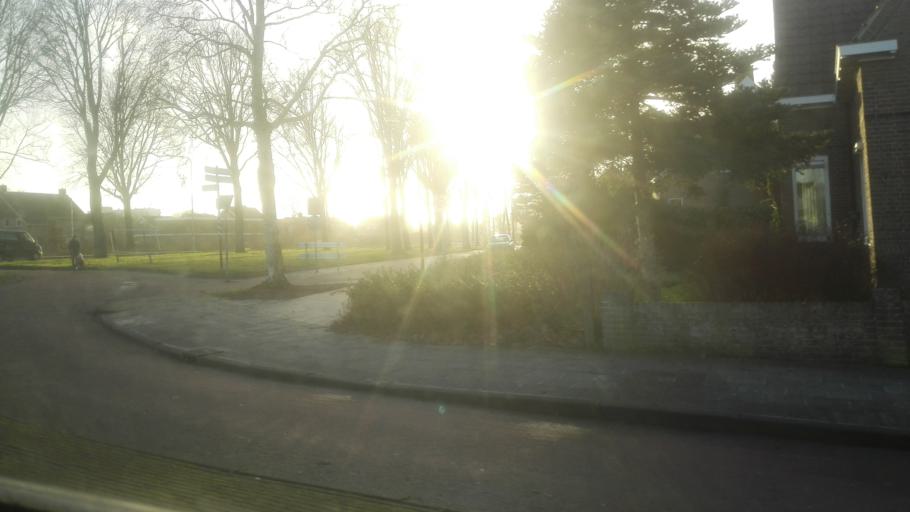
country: NL
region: Friesland
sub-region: Gemeente Heerenveen
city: Oranjewoud
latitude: 52.9505
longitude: 5.9347
